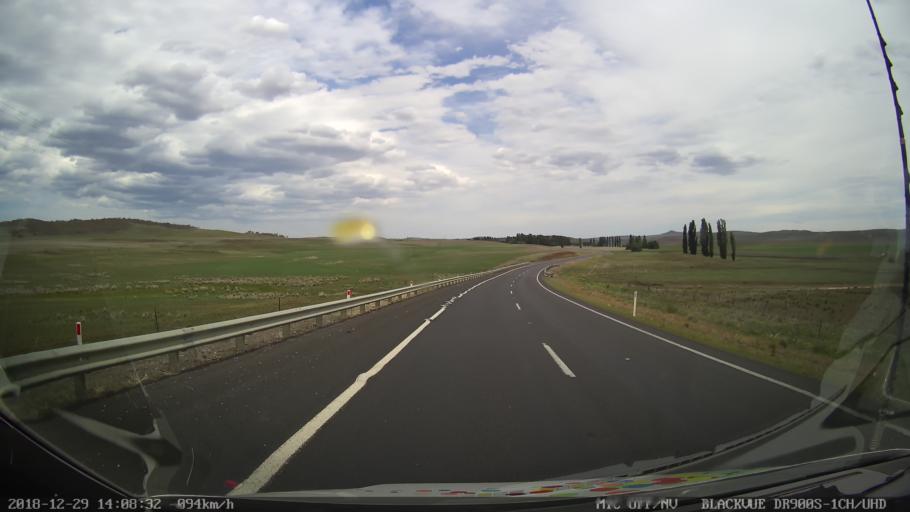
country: AU
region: New South Wales
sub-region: Cooma-Monaro
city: Cooma
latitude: -36.3666
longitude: 149.2146
